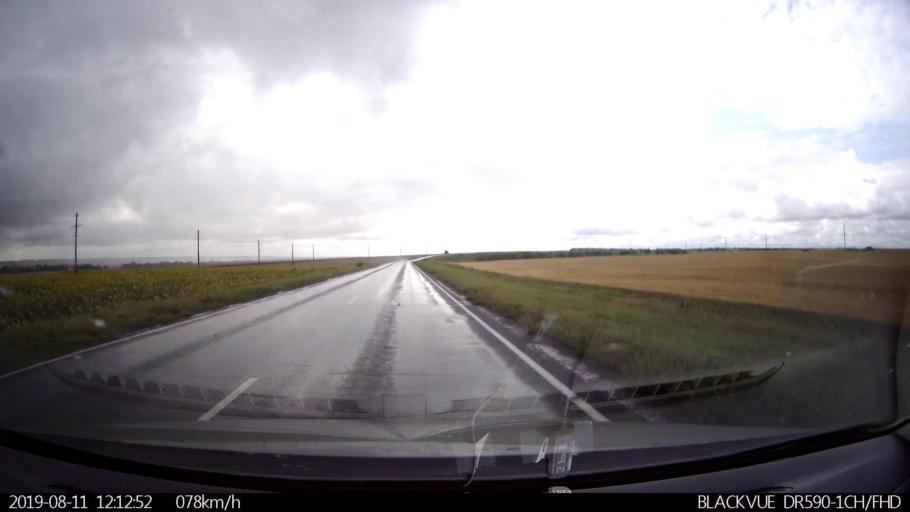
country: RU
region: Ulyanovsk
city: Silikatnyy
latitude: 53.9680
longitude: 47.9948
